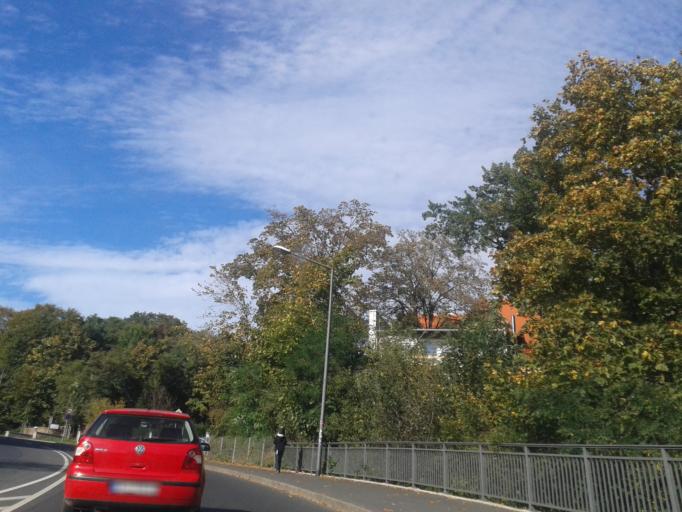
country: DE
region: Saxony
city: Albertstadt
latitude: 51.0971
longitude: 13.7189
